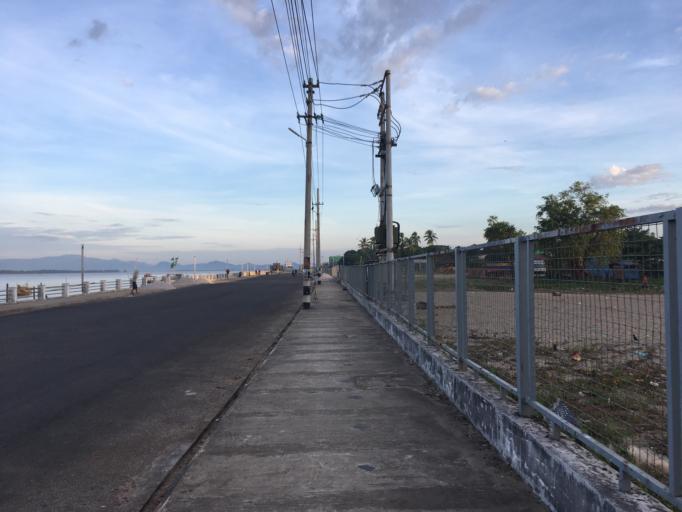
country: MM
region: Mon
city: Mawlamyine
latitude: 16.4611
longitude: 97.6230
